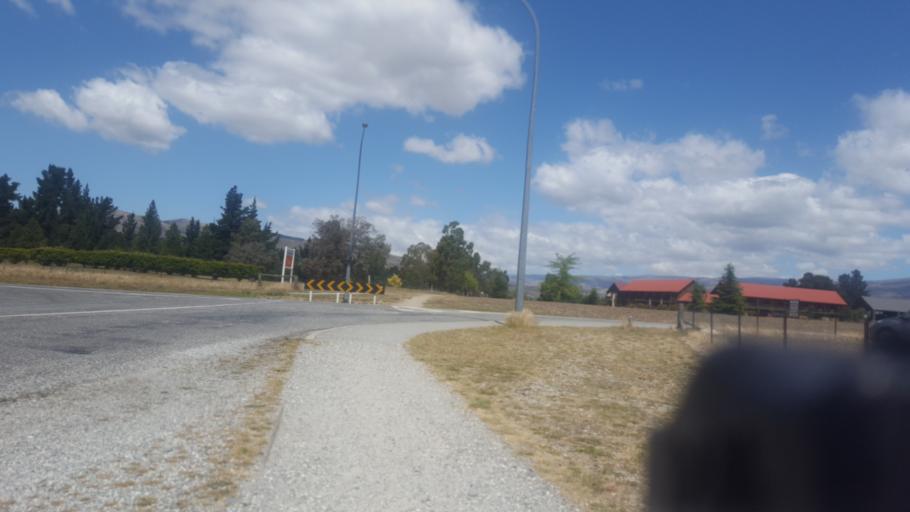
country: NZ
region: Otago
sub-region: Queenstown-Lakes District
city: Wanaka
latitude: -45.0341
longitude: 169.2022
